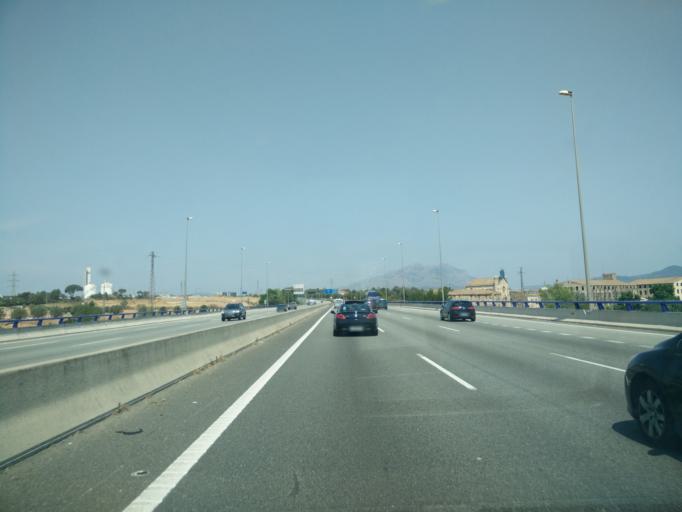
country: ES
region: Catalonia
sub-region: Provincia de Barcelona
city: Martorell
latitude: 41.4943
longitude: 1.9232
